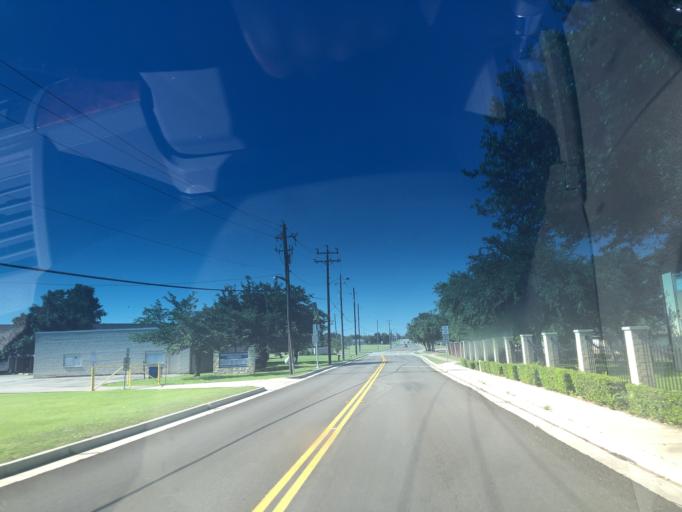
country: US
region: Texas
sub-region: Dallas County
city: Grand Prairie
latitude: 32.7149
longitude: -97.0196
